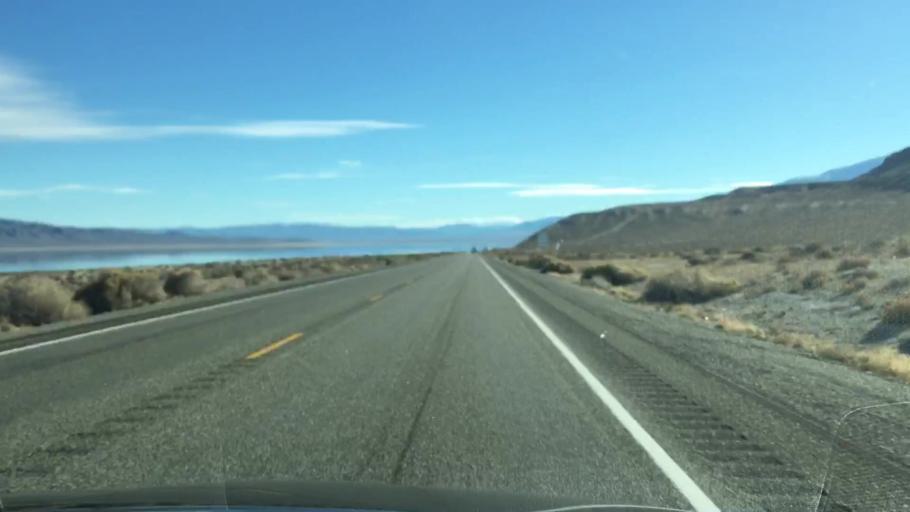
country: US
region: Nevada
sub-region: Mineral County
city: Hawthorne
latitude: 38.7905
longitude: -118.7551
